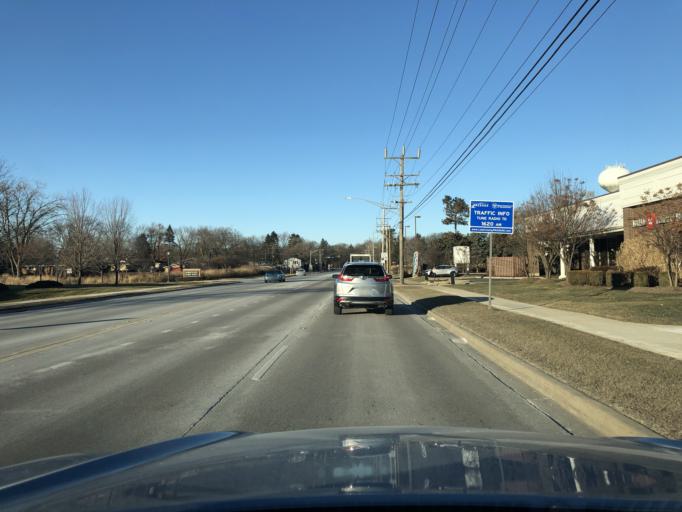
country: US
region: Illinois
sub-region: Cook County
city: Barrington
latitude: 42.1571
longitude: -88.1283
